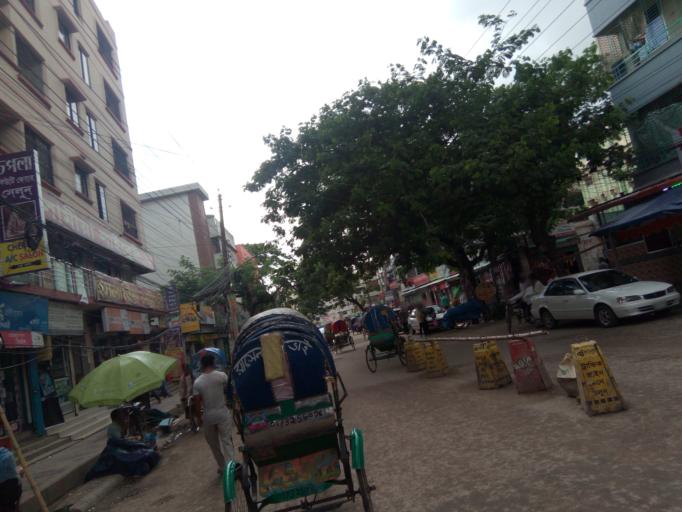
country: BD
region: Dhaka
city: Azimpur
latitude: 23.7617
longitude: 90.3566
